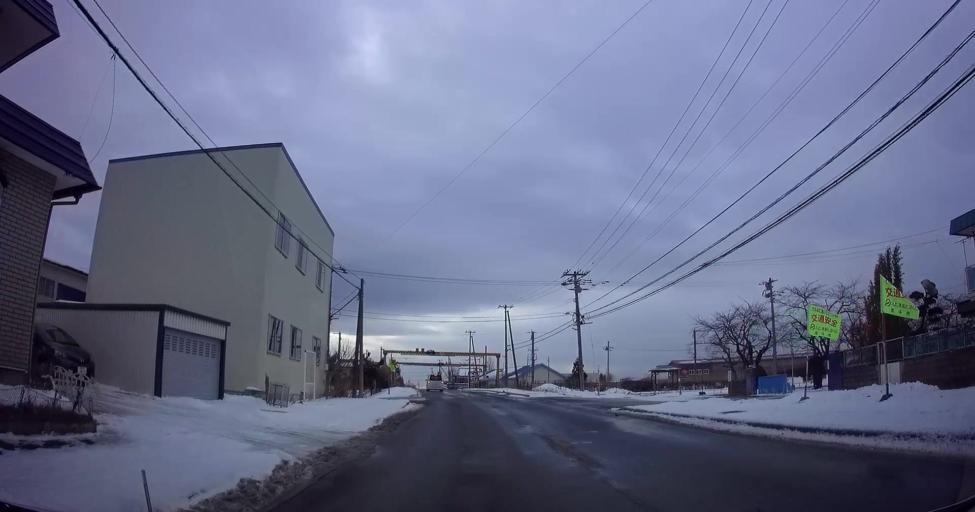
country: JP
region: Hokkaido
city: Kamiiso
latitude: 41.8263
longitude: 140.6856
